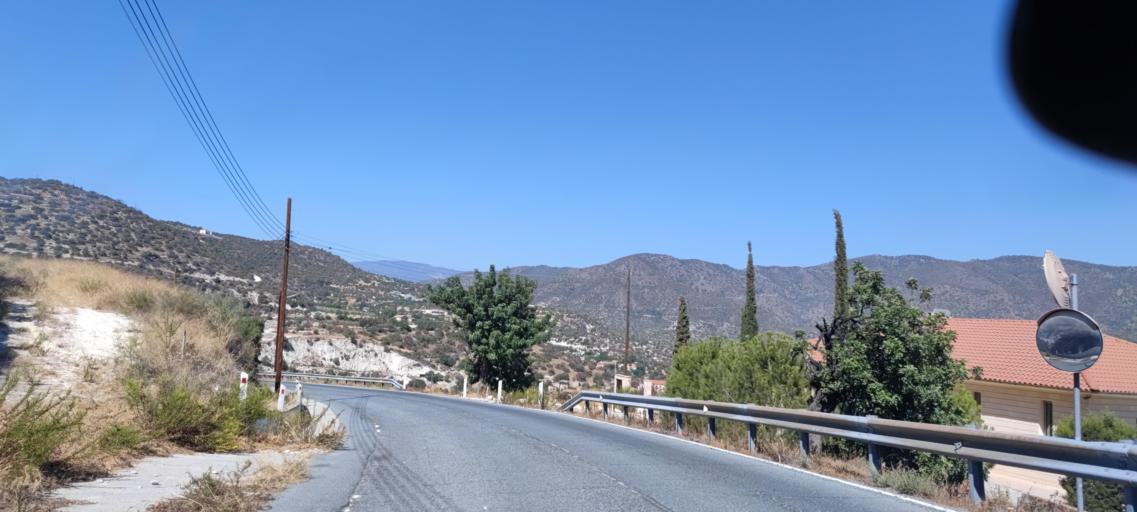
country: CY
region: Limassol
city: Mouttagiaka
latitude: 34.7675
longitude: 33.0571
